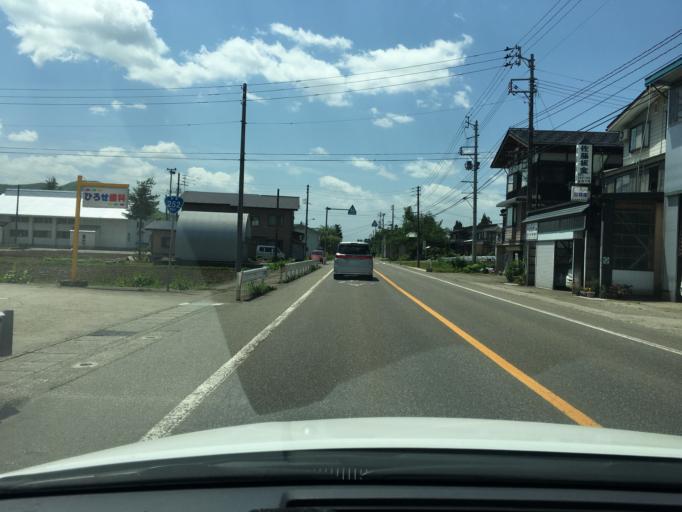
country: JP
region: Niigata
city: Tochio-honcho
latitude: 37.2896
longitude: 138.9889
